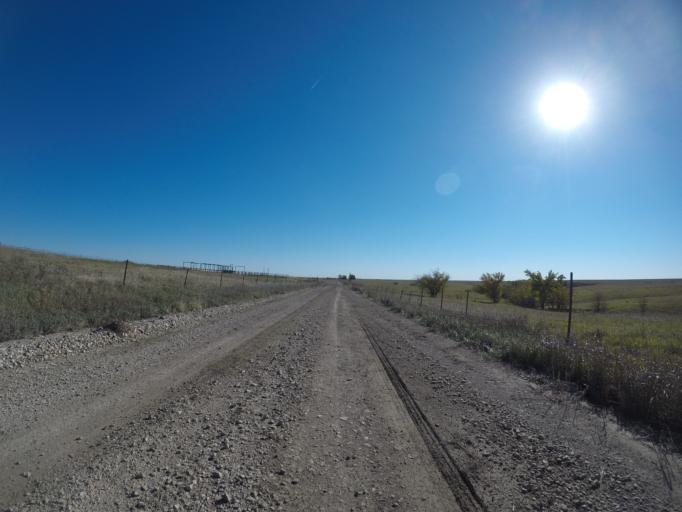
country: US
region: Kansas
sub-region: Wabaunsee County
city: Alma
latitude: 38.8842
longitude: -96.4037
